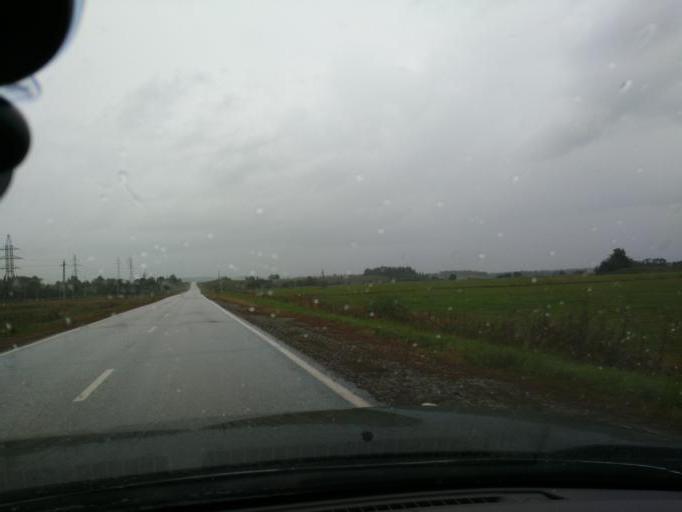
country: RU
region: Perm
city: Barda
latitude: 57.0866
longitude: 55.5401
